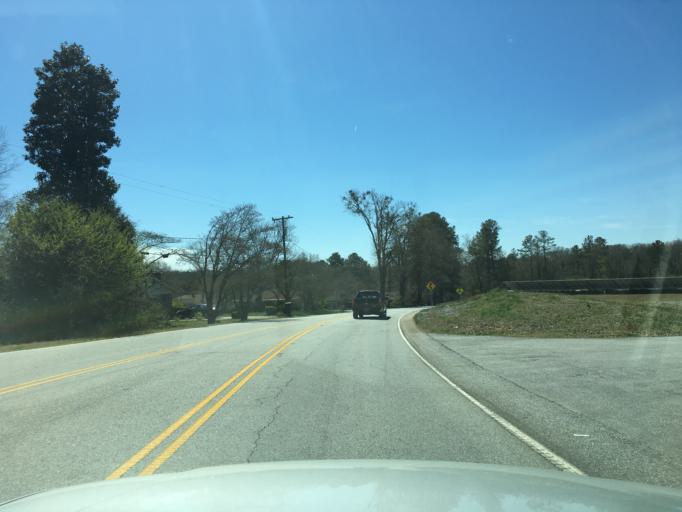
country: US
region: South Carolina
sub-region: Spartanburg County
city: Roebuck
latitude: 34.9079
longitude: -81.9593
